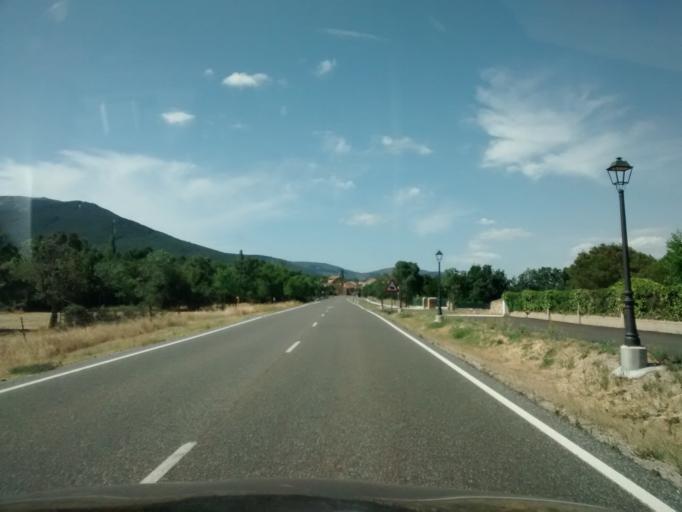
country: ES
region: Castille and Leon
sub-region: Provincia de Segovia
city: Collado Hermoso
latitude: 41.0429
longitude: -3.9154
